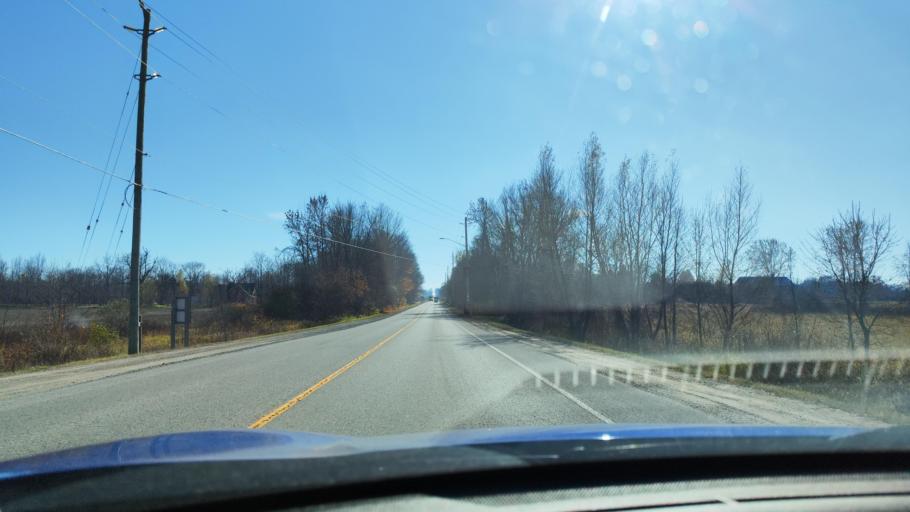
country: CA
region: Ontario
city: Wasaga Beach
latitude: 44.4741
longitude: -80.0067
